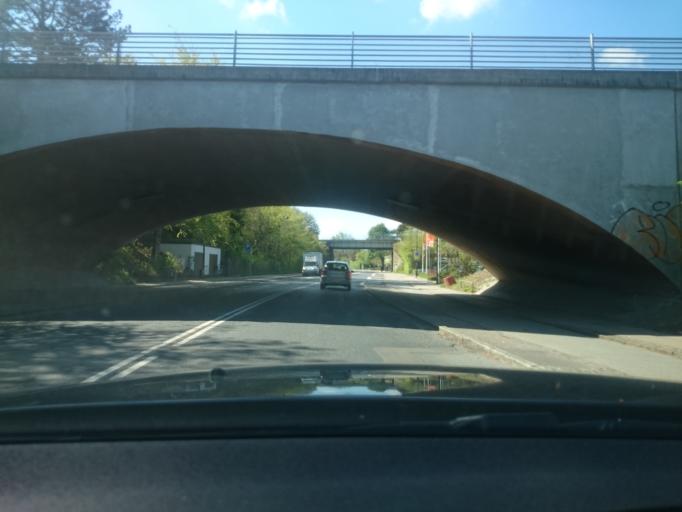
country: DK
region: Capital Region
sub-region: Lyngby-Tarbaek Kommune
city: Kongens Lyngby
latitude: 55.7572
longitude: 12.5359
